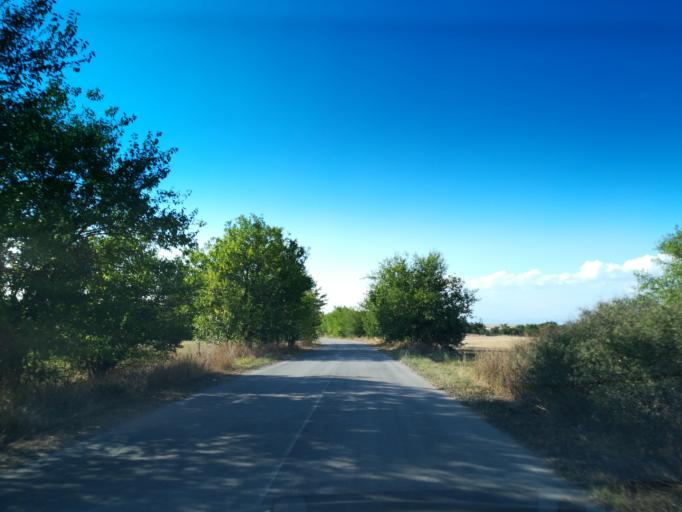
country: BG
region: Stara Zagora
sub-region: Obshtina Chirpan
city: Chirpan
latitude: 42.0552
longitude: 25.2703
